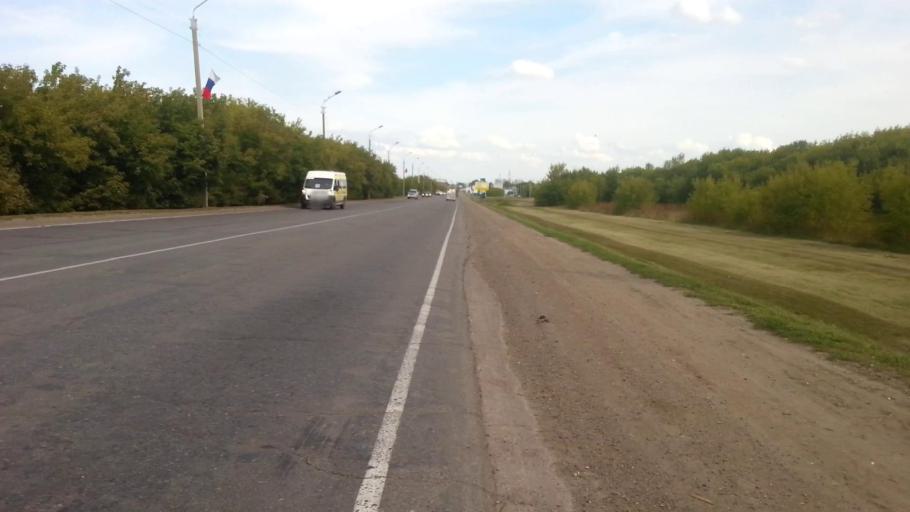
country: RU
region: Altai Krai
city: Novosilikatnyy
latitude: 53.3506
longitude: 83.6007
